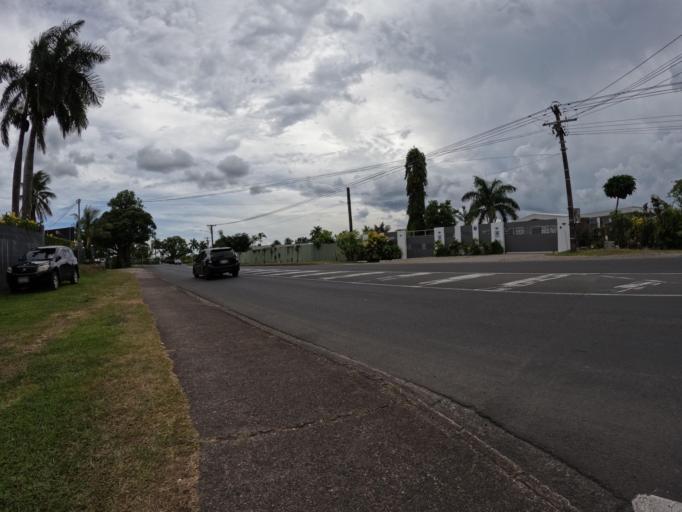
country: FJ
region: Central
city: Suva
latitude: -18.1152
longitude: 178.4383
